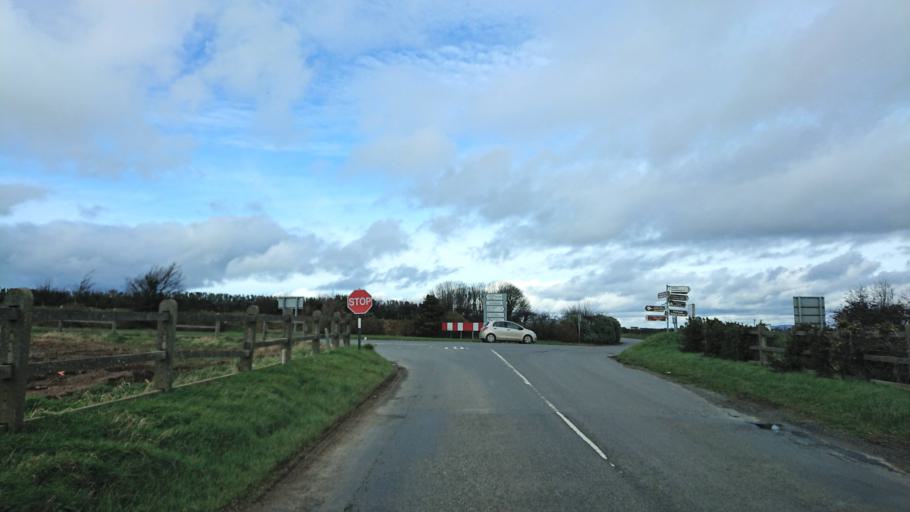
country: IE
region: Munster
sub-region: Waterford
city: Dunmore East
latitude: 52.2448
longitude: -6.9084
